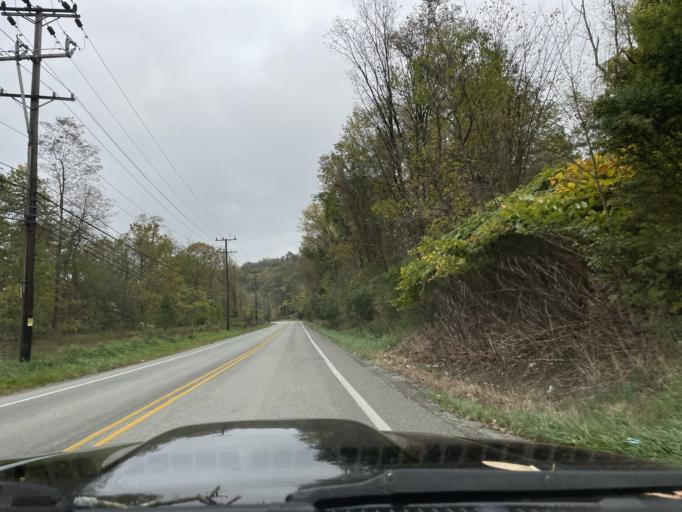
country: US
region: Pennsylvania
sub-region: Allegheny County
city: Cheswick
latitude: 40.5284
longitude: -79.8010
